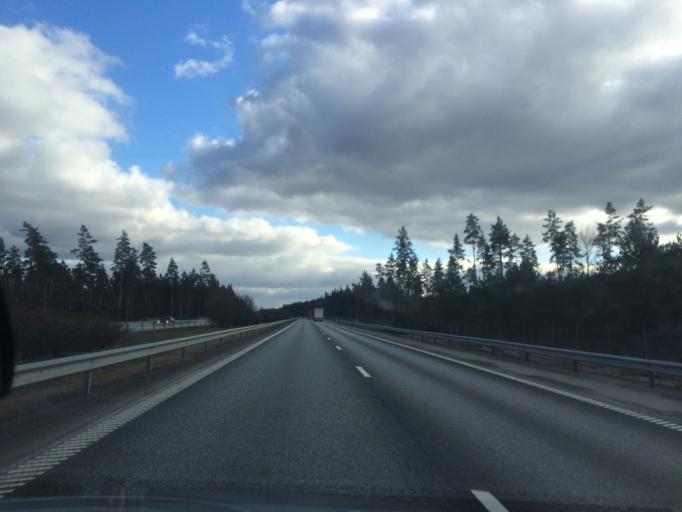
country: SE
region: Joenkoeping
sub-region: Vaggeryds Kommun
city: Skillingaryd
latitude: 57.3802
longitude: 14.1000
